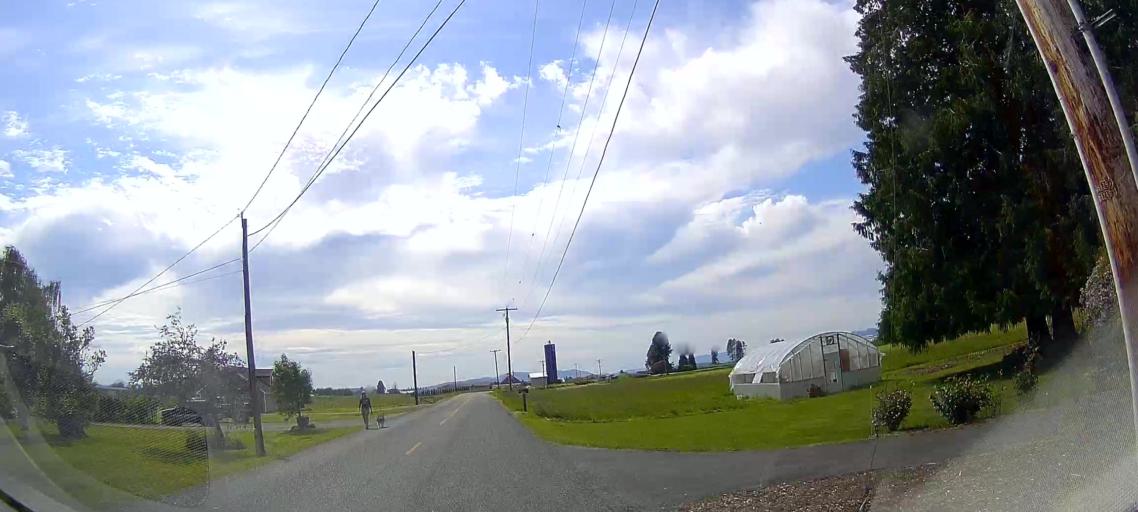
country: US
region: Washington
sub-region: Skagit County
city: Burlington
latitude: 48.5356
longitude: -122.3834
